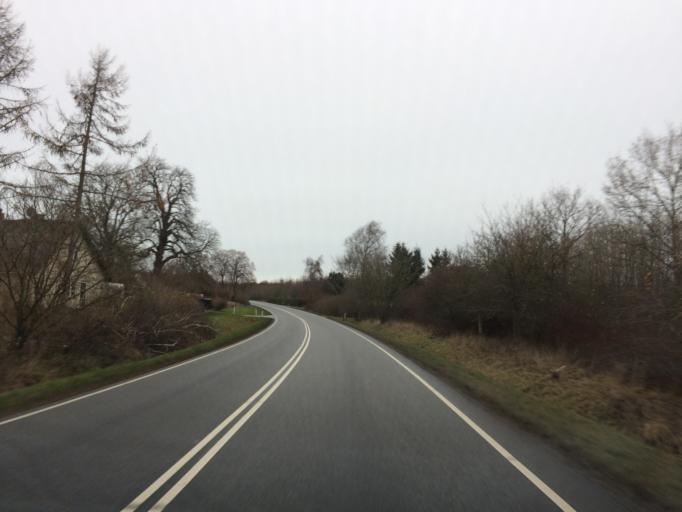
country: DK
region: Zealand
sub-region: Holbaek Kommune
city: Jyderup
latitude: 55.6217
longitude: 11.3975
